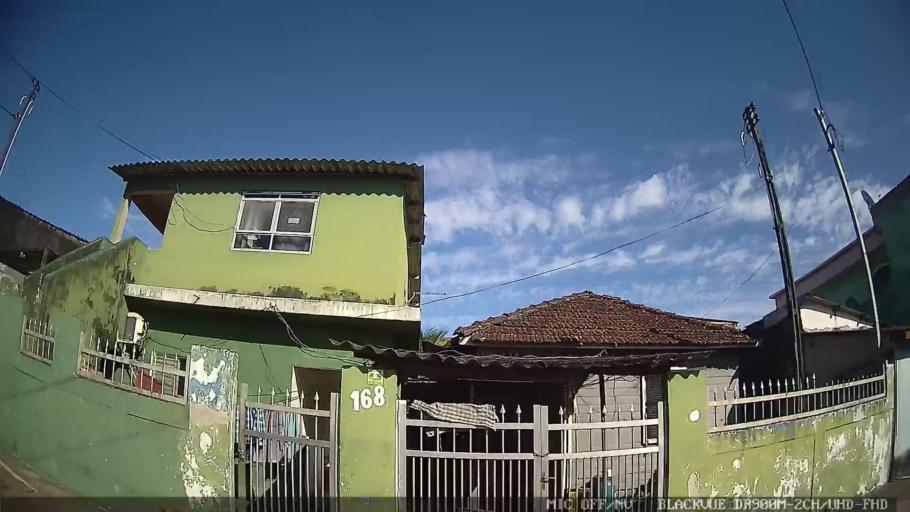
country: BR
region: Sao Paulo
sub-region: Santos
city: Santos
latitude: -23.9479
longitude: -46.2987
